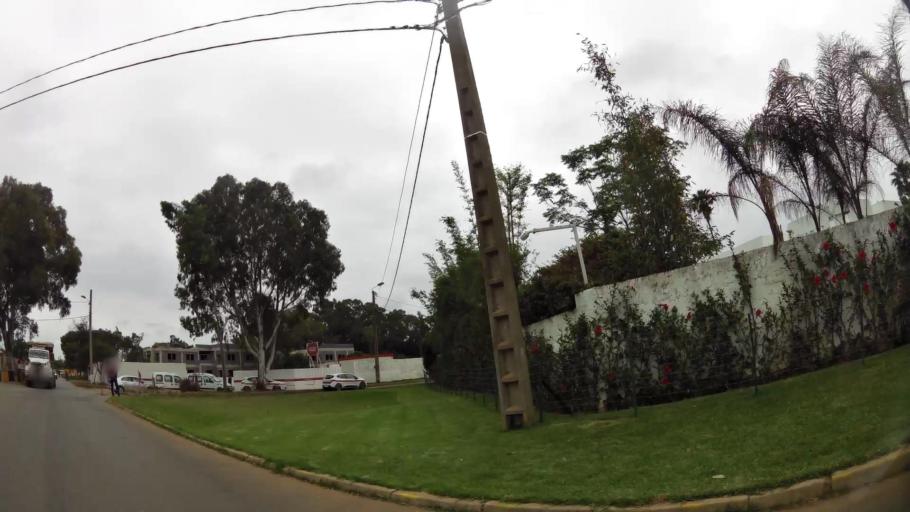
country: MA
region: Rabat-Sale-Zemmour-Zaer
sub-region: Rabat
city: Rabat
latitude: 33.9638
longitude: -6.8193
